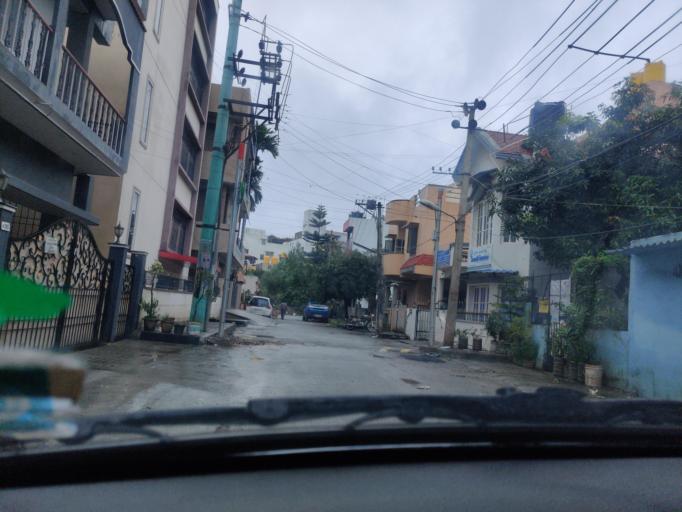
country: IN
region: Karnataka
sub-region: Bangalore Urban
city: Bangalore
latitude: 13.0276
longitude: 77.6351
